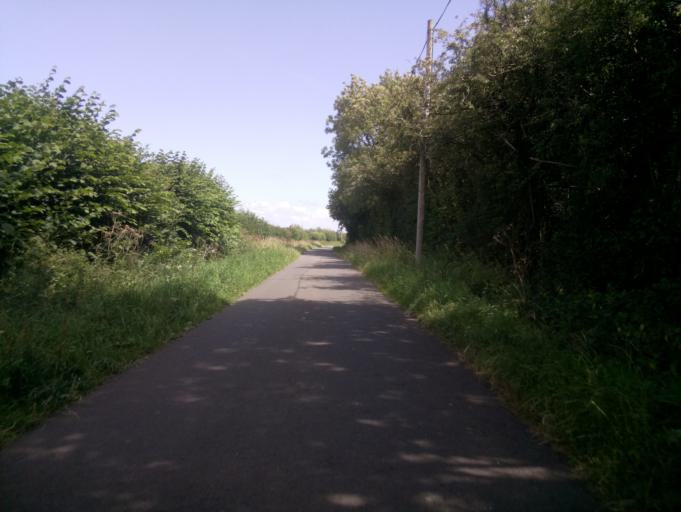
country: GB
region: England
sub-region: Wiltshire
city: Norton
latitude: 51.5168
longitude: -2.1893
